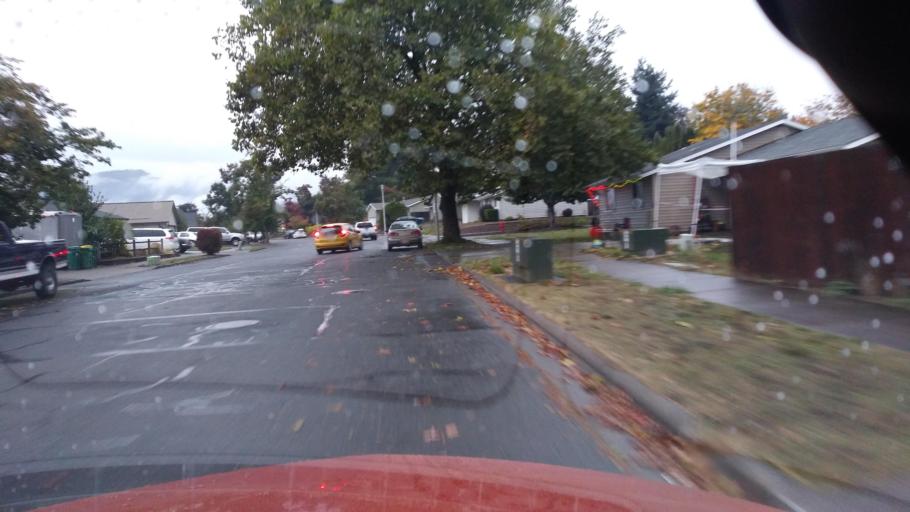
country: US
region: Oregon
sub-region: Washington County
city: Forest Grove
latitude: 45.5276
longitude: -123.1339
